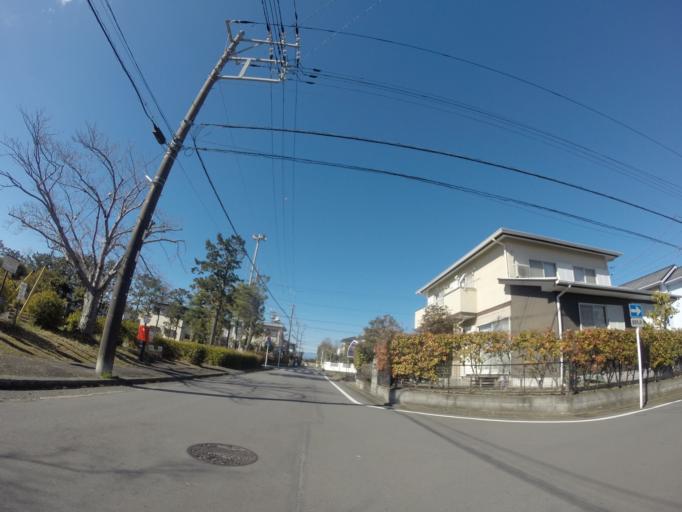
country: JP
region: Shizuoka
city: Numazu
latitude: 35.1361
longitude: 138.8022
